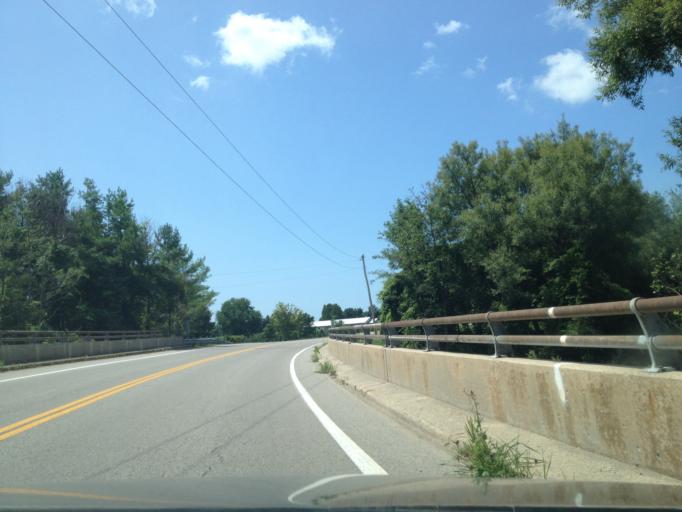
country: CA
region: Ontario
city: Norfolk County
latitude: 42.5948
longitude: -80.4852
